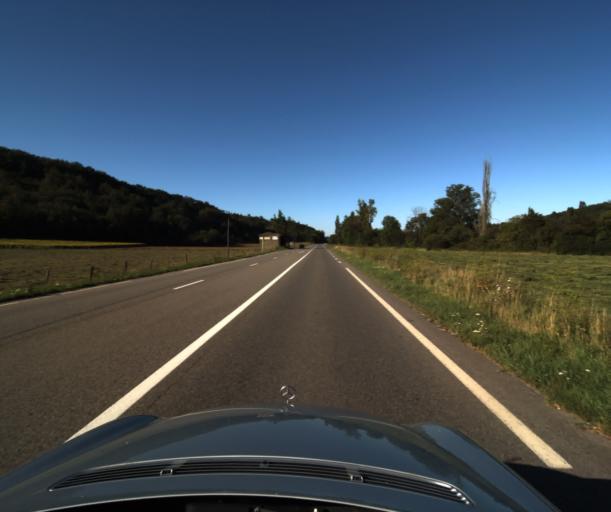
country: FR
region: Midi-Pyrenees
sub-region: Departement de l'Ariege
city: Mirepoix
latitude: 43.0086
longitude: 1.8855
